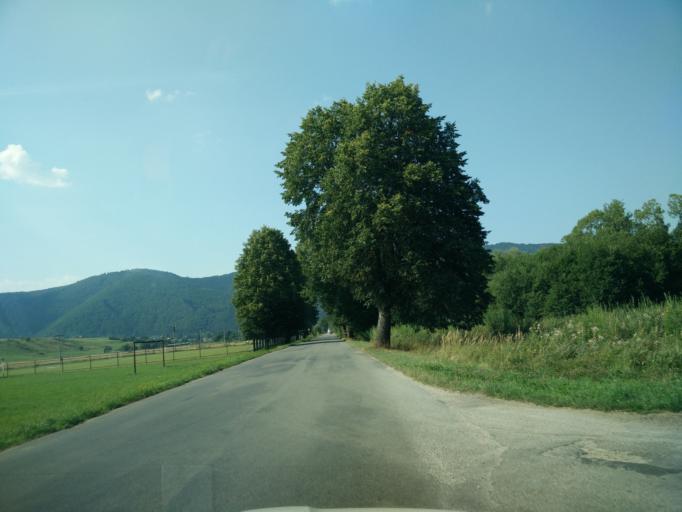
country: SK
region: Zilinsky
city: Rajec
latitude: 49.1140
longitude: 18.6904
